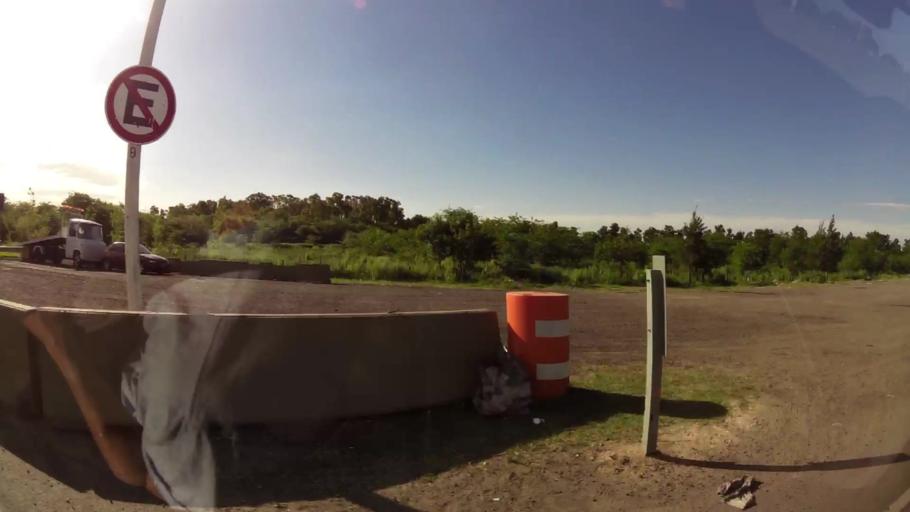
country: AR
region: Buenos Aires
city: Hurlingham
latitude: -34.5653
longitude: -58.6323
